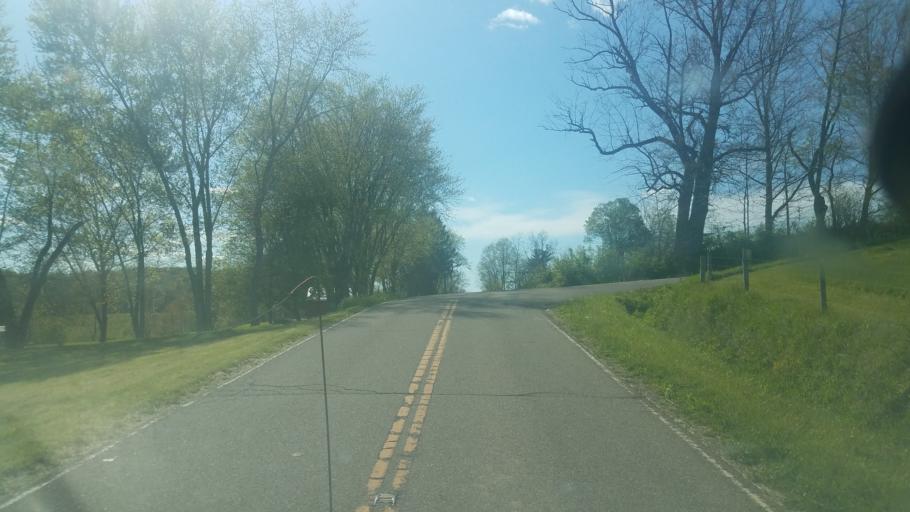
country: US
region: Ohio
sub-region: Coshocton County
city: Coshocton
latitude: 40.3316
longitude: -81.8977
